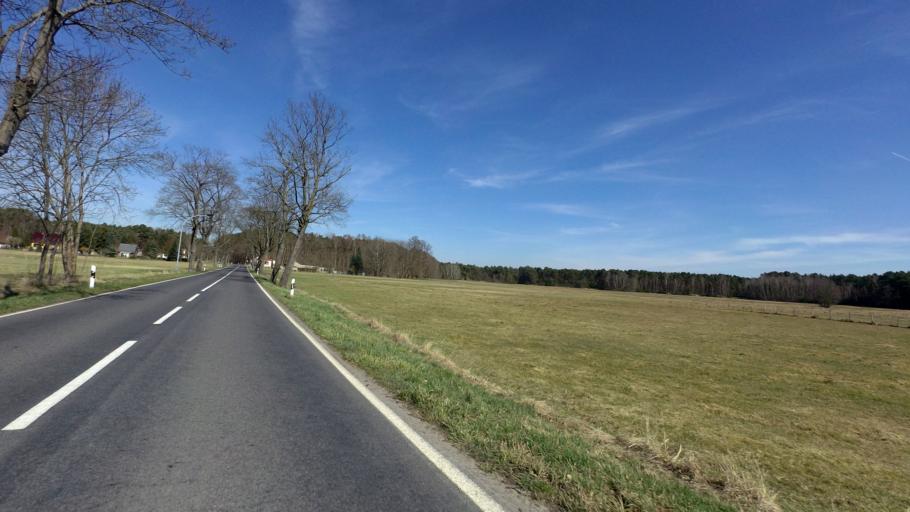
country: DE
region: Brandenburg
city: Storkow
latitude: 52.1956
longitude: 13.9206
